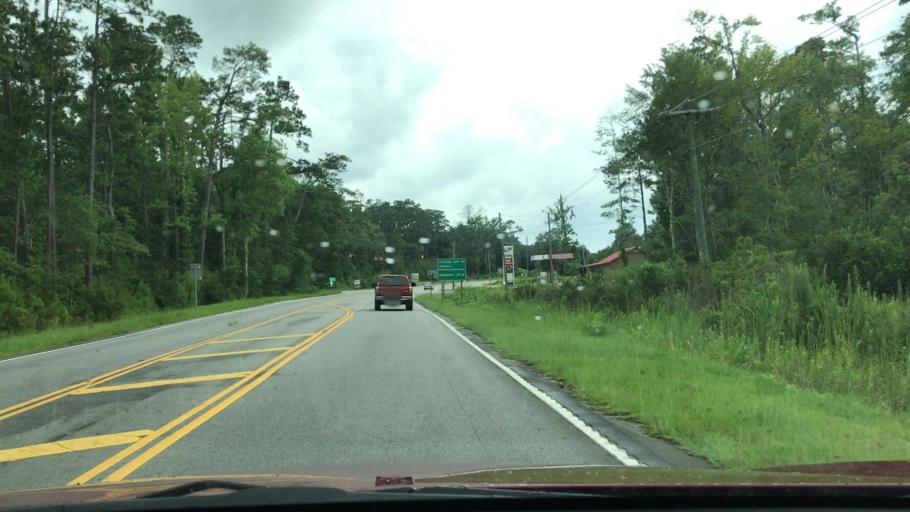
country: US
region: South Carolina
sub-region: Georgetown County
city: Georgetown
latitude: 33.4838
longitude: -79.2684
